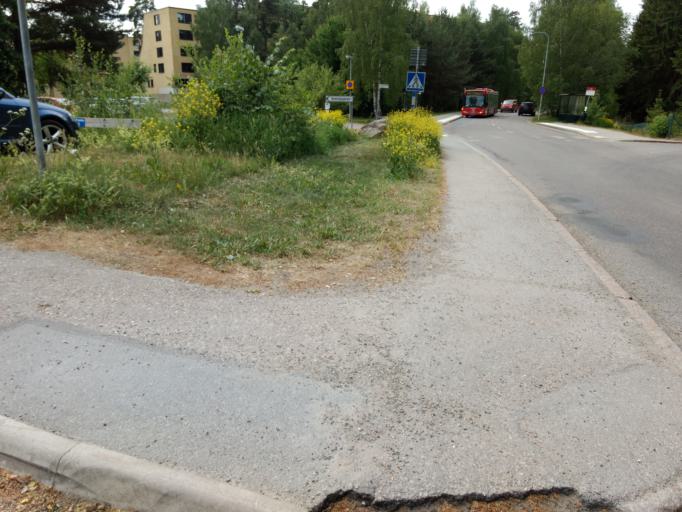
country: SE
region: Stockholm
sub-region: Upplands Vasby Kommun
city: Upplands Vaesby
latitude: 59.5296
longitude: 17.9094
